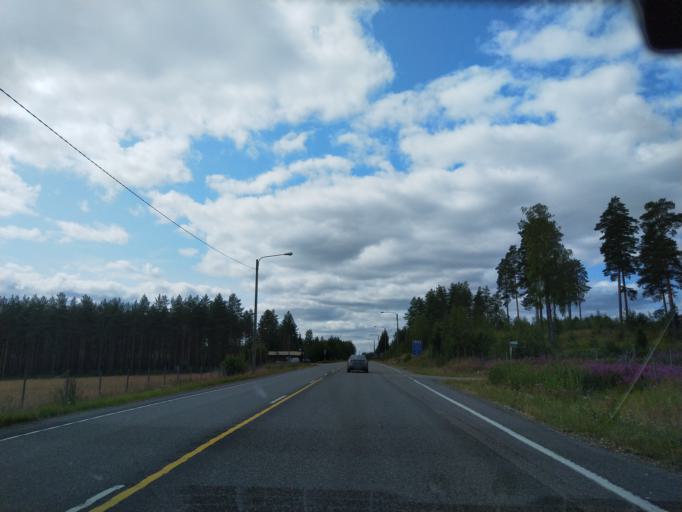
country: FI
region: Haeme
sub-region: Riihimaeki
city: Loppi
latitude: 60.7283
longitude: 24.5222
